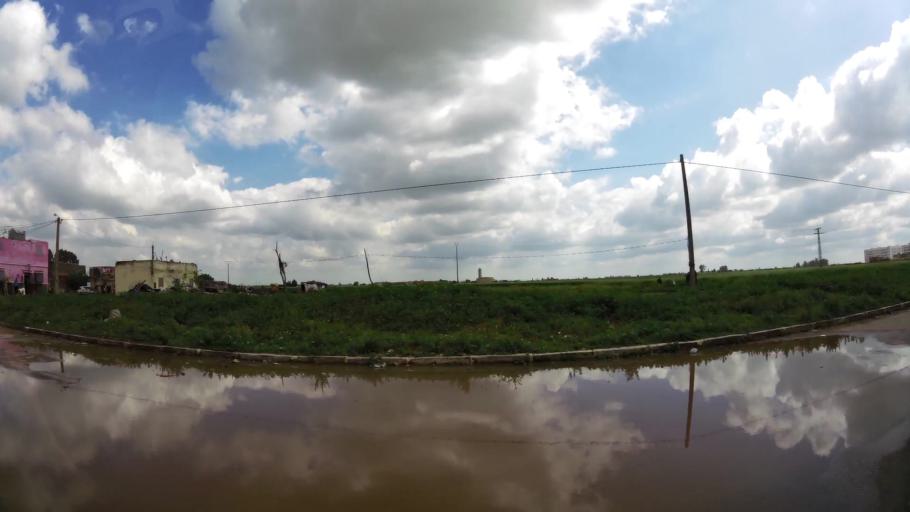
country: MA
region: Chaouia-Ouardigha
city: Nouaseur
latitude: 33.3622
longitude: -7.5334
